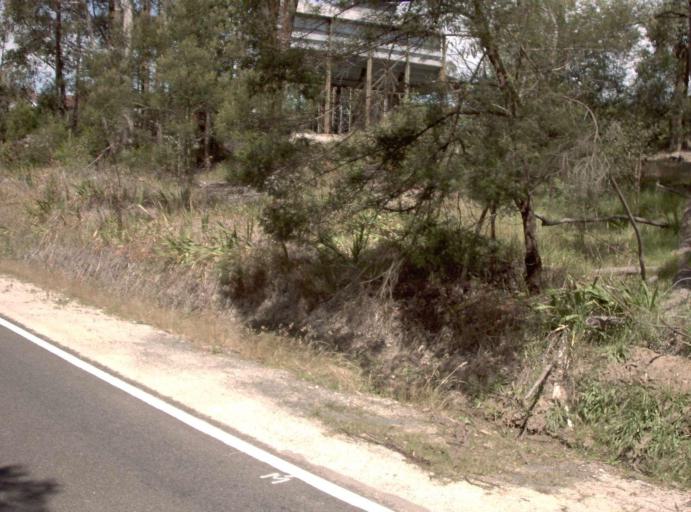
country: AU
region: New South Wales
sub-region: Bombala
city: Bombala
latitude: -37.5641
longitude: 149.1579
